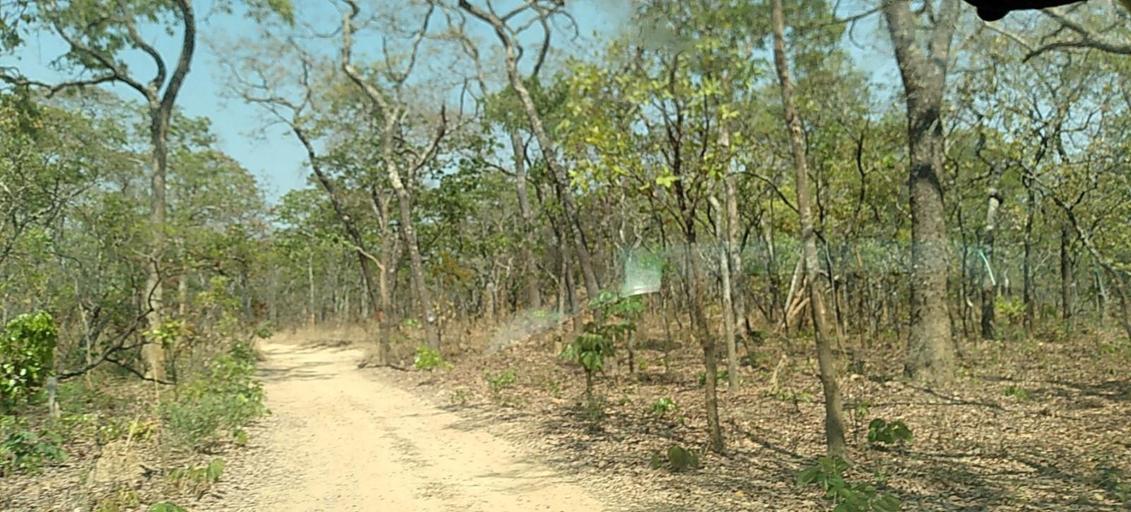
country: ZM
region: North-Western
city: Kasempa
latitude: -13.3915
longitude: 25.6266
